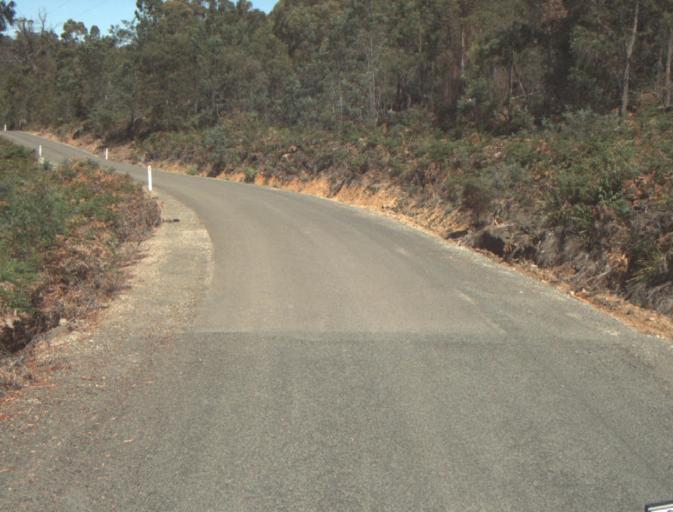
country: AU
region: Tasmania
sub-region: Launceston
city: Mayfield
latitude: -41.3207
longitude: 147.1226
